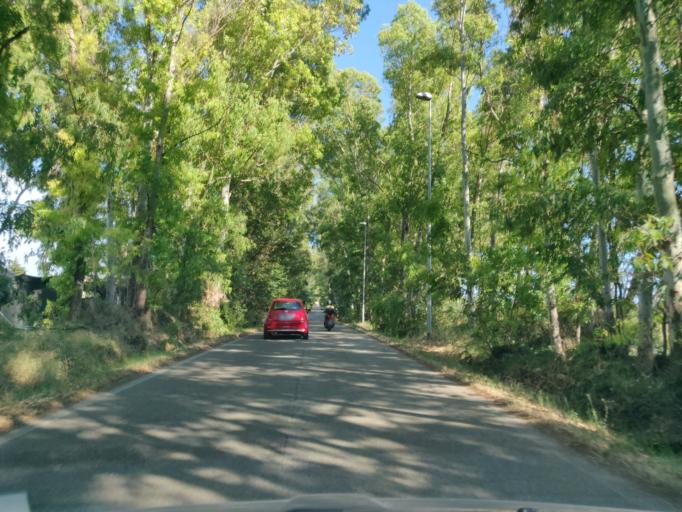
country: IT
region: Latium
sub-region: Citta metropolitana di Roma Capitale
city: Aurelia
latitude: 42.1602
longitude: 11.7485
